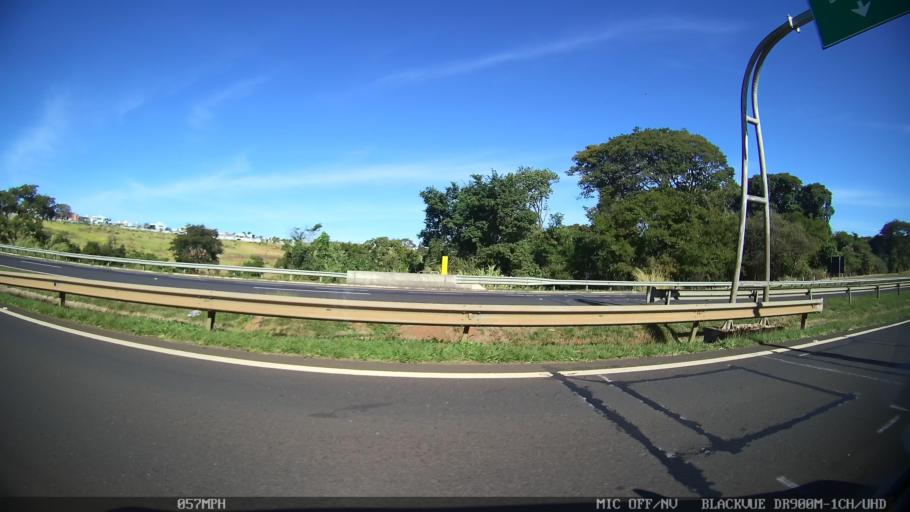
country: BR
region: Sao Paulo
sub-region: Franca
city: Franca
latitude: -20.5639
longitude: -47.4108
